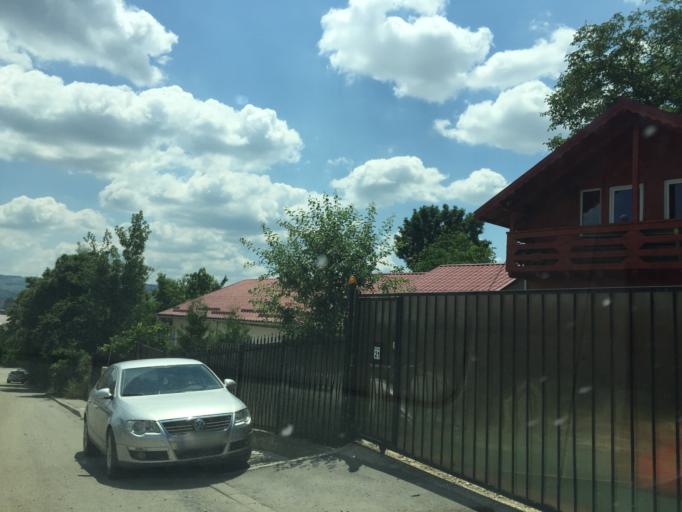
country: RO
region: Cluj
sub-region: Municipiul Cluj-Napoca
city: Cluj-Napoca
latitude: 46.7982
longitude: 23.6021
